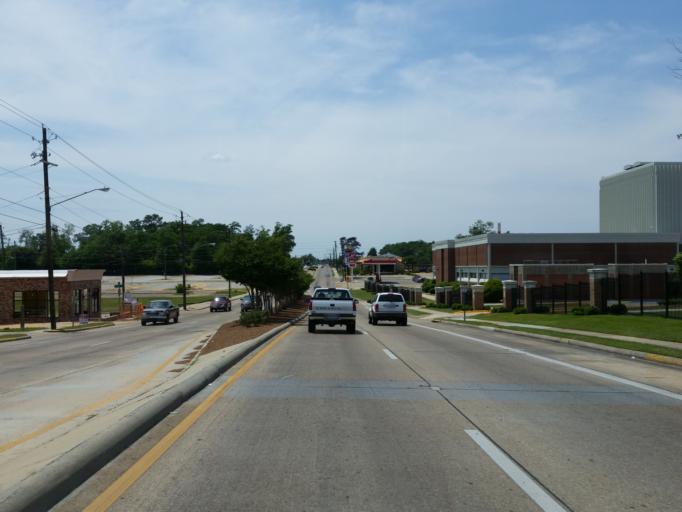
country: US
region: Mississippi
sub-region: Lamar County
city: Arnold Line
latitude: 31.3248
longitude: -89.3334
